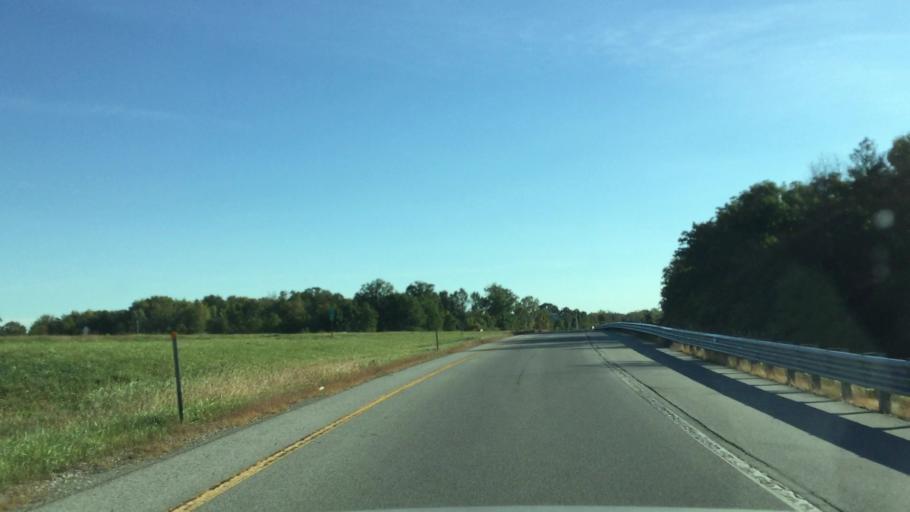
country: US
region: Michigan
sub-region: Genesee County
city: Beecher
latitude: 43.0961
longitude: -83.7320
